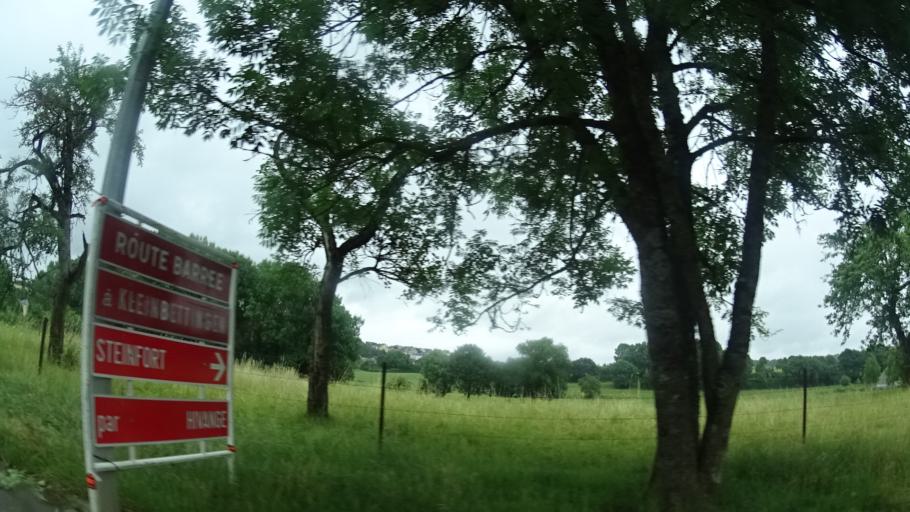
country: LU
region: Luxembourg
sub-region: Canton de Capellen
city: Clemency
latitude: 49.5924
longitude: 5.8787
